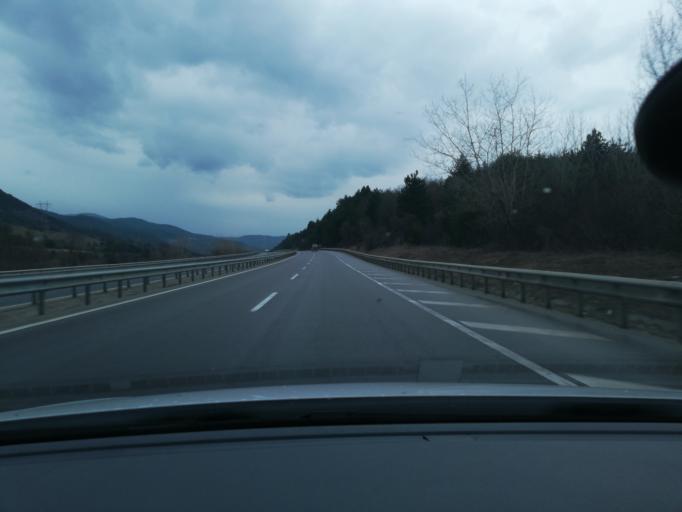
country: TR
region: Bolu
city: Yenicaga
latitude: 40.7486
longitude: 31.8856
